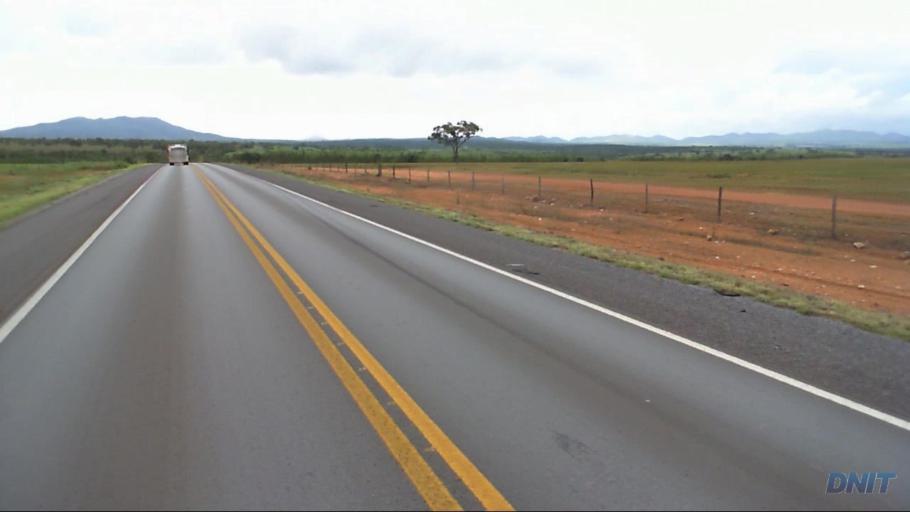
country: BR
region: Goias
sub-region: Padre Bernardo
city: Padre Bernardo
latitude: -15.2198
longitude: -48.6394
